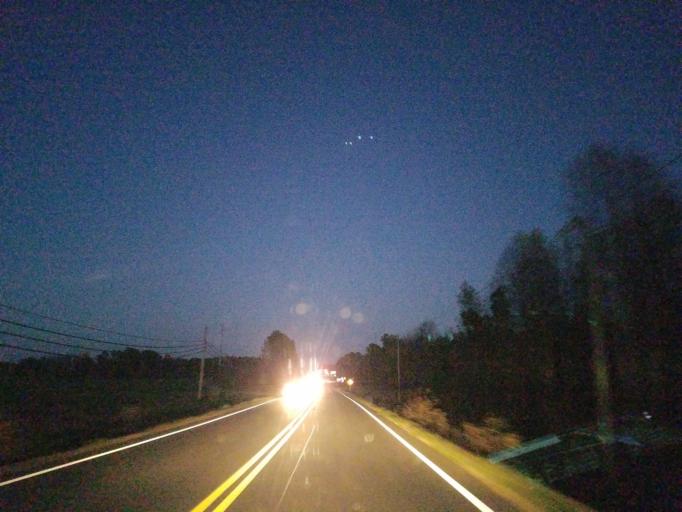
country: US
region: Georgia
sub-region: Forsyth County
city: Cumming
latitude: 34.2511
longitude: -84.0989
